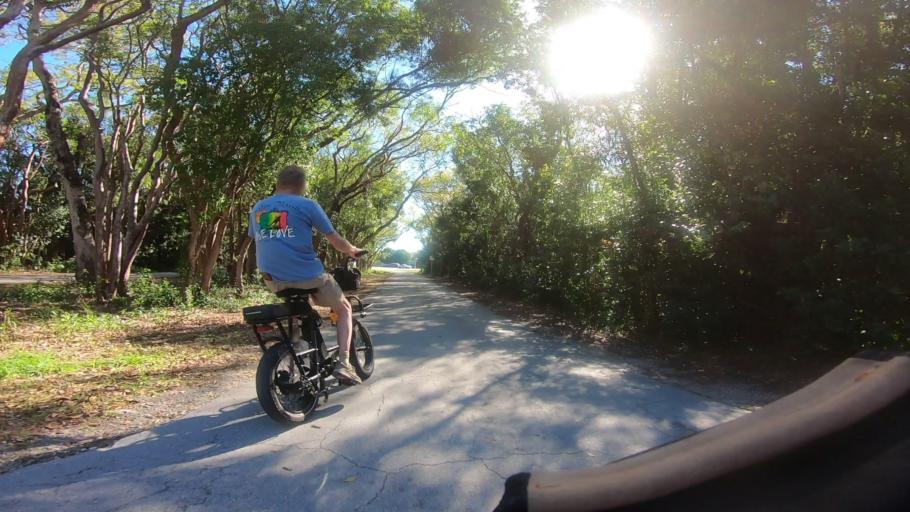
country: US
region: Florida
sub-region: Monroe County
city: Key Largo
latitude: 25.1115
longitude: -80.4257
